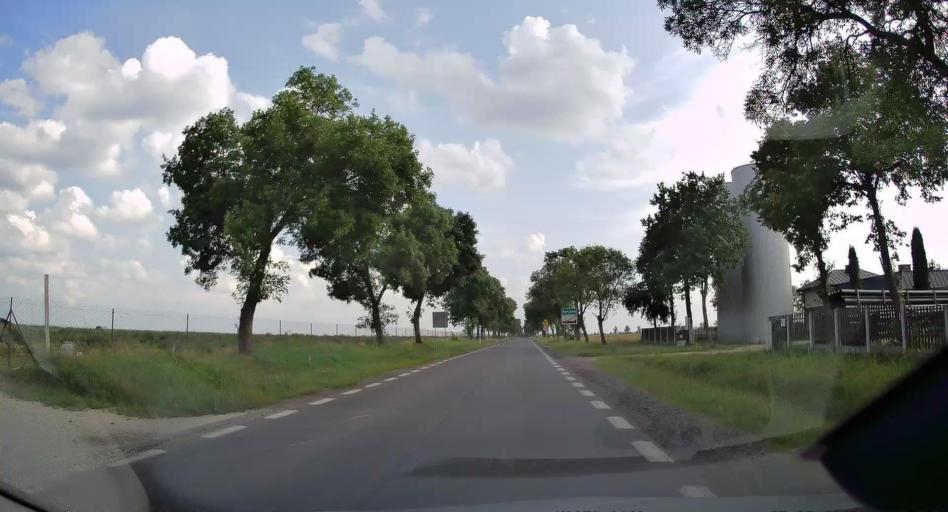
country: PL
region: Lodz Voivodeship
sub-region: Powiat tomaszowski
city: Rzeczyca
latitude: 51.6262
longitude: 20.2927
